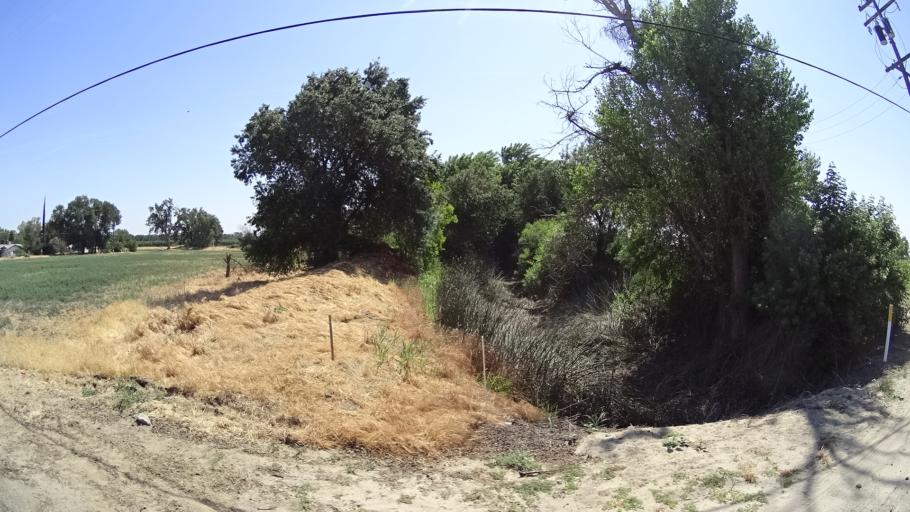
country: US
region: California
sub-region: Kings County
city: Lemoore
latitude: 36.3323
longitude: -119.8513
